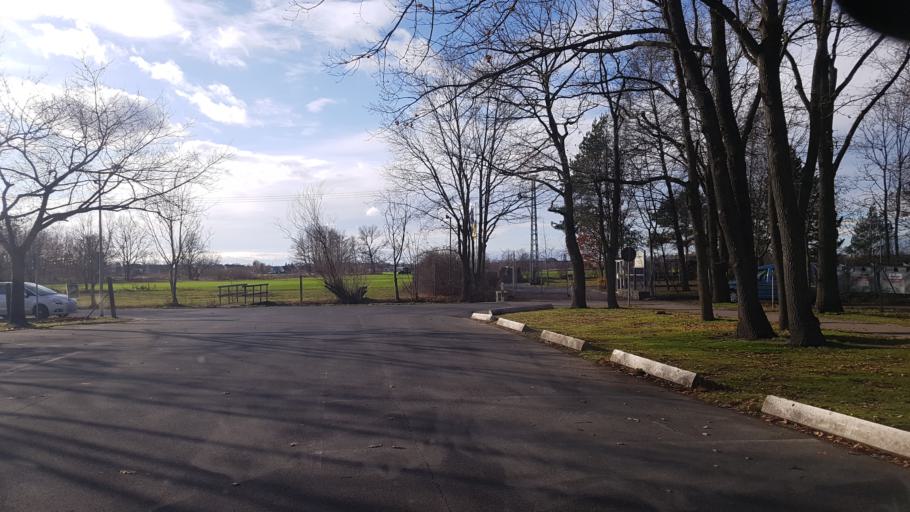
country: DE
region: Brandenburg
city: Falkenberg
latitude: 51.5942
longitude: 13.2594
